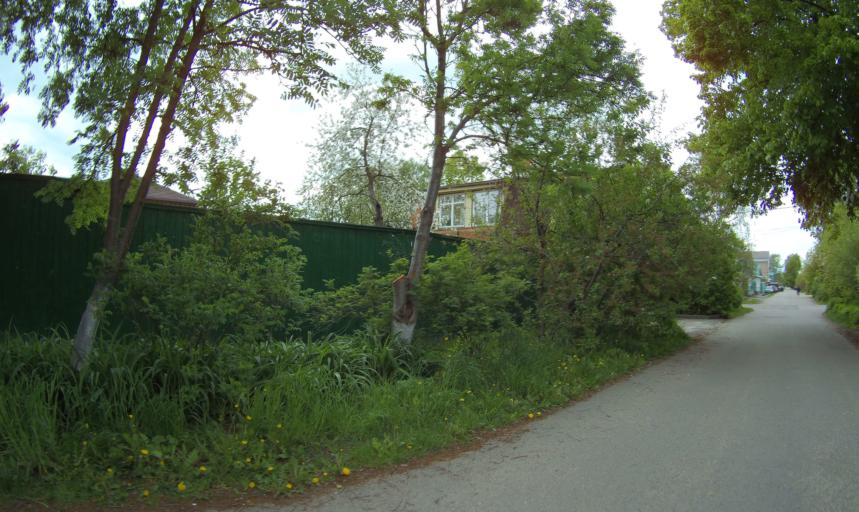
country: RU
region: Moskovskaya
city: Kolomna
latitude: 55.0989
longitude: 38.7490
